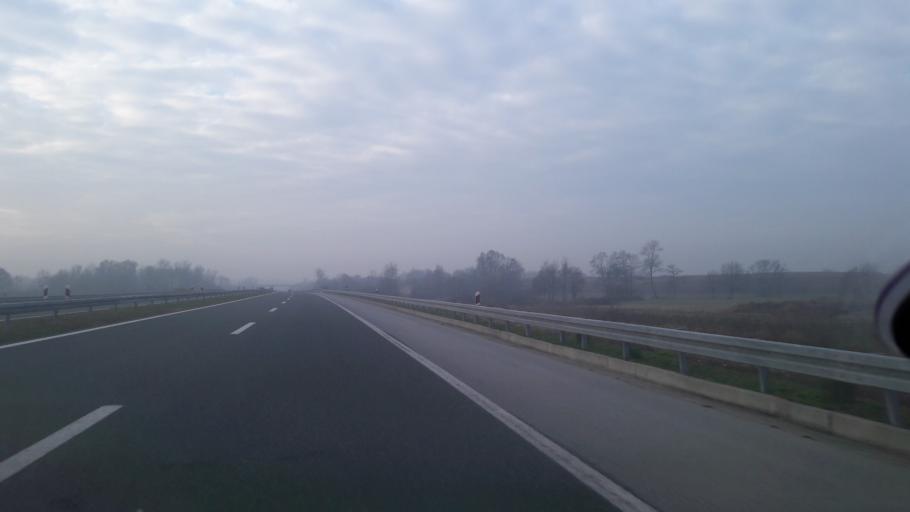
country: HR
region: Osjecko-Baranjska
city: Piskorevci
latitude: 45.3075
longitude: 18.3651
